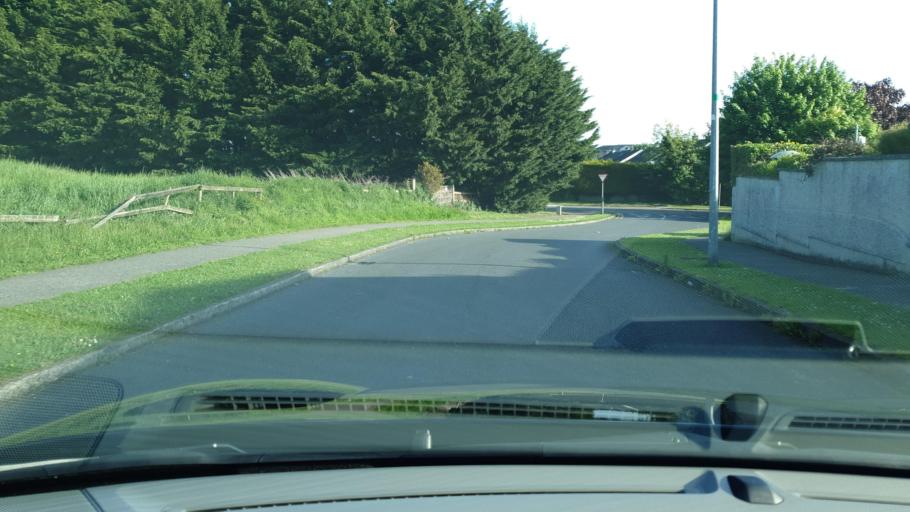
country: IE
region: Leinster
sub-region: An Mhi
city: Ashbourne
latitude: 53.5167
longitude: -6.3997
